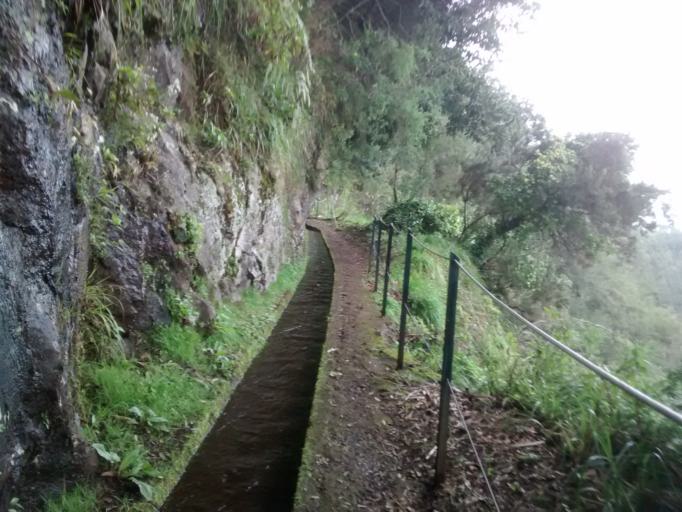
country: PT
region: Madeira
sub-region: Santana
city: Santana
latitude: 32.8103
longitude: -16.9320
